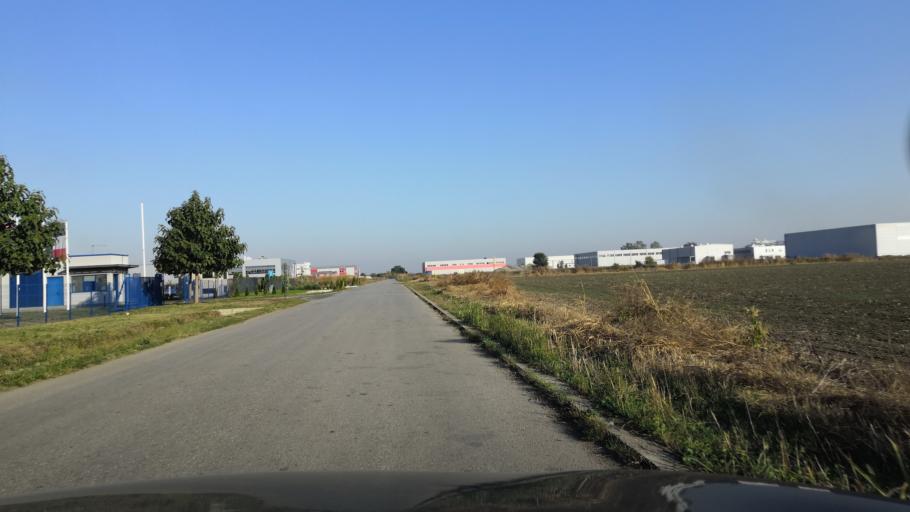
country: RS
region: Autonomna Pokrajina Vojvodina
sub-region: Sremski Okrug
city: Stara Pazova
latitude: 44.9900
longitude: 20.1963
